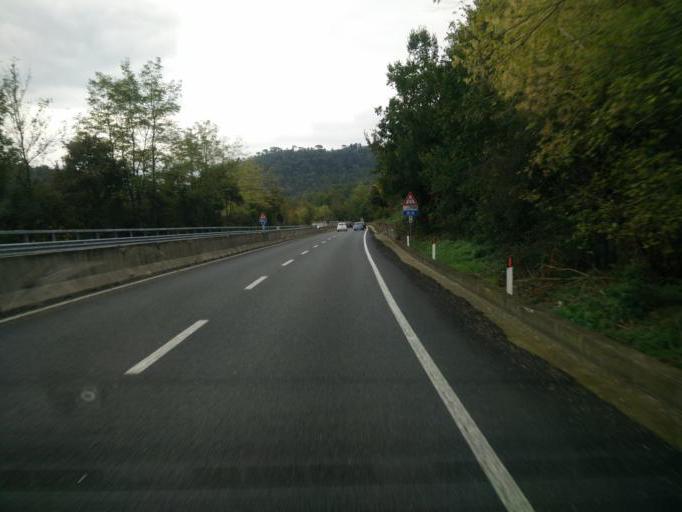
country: IT
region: Tuscany
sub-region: Province of Florence
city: San Casciano in Val di Pesa
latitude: 43.6778
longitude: 11.2107
